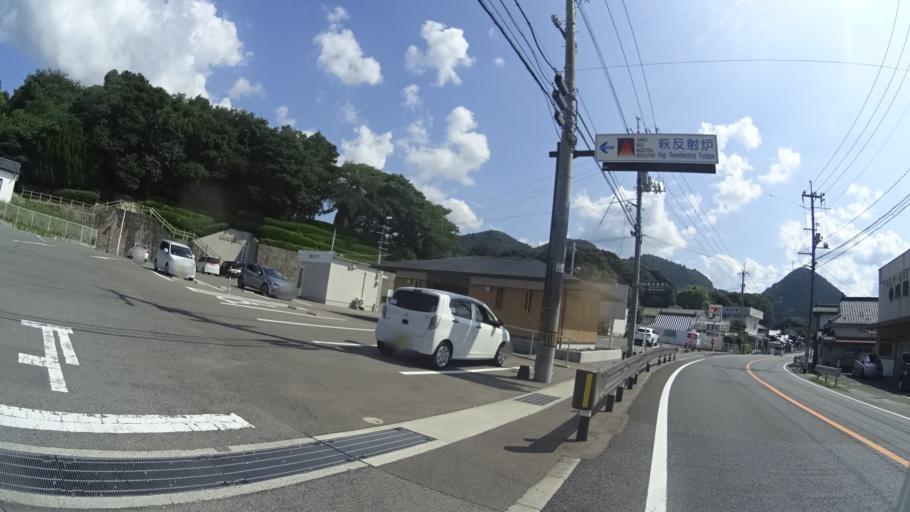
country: JP
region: Yamaguchi
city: Hagi
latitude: 34.4286
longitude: 131.4175
